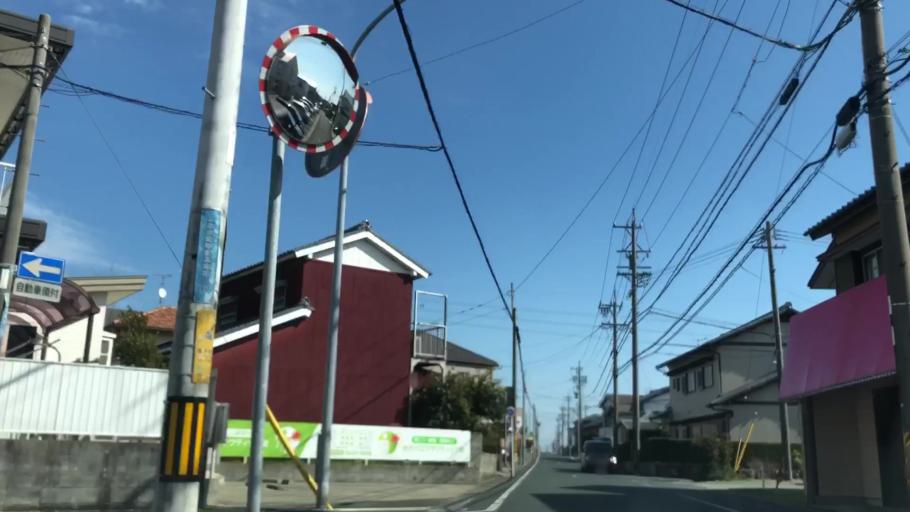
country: JP
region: Aichi
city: Toyohashi
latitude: 34.7233
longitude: 137.3985
